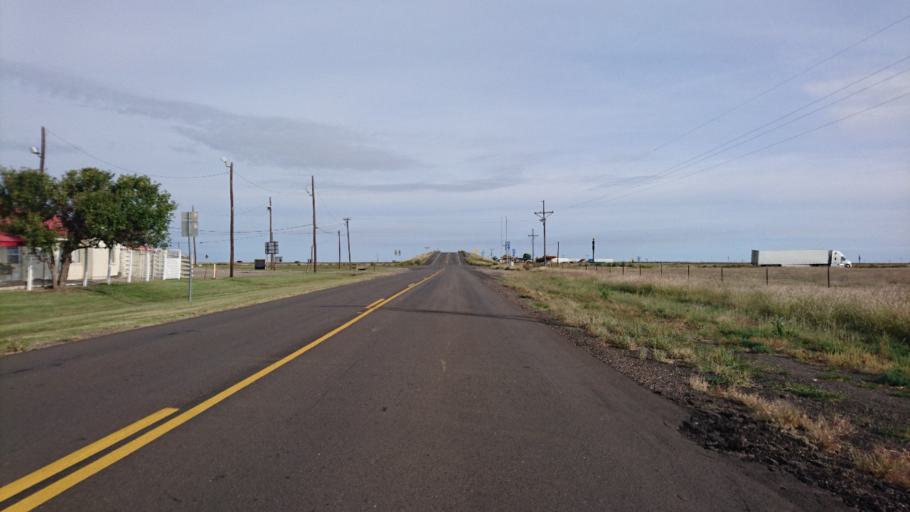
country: US
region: Texas
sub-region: Armstrong County
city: Claude
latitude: 35.2140
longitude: -101.3825
